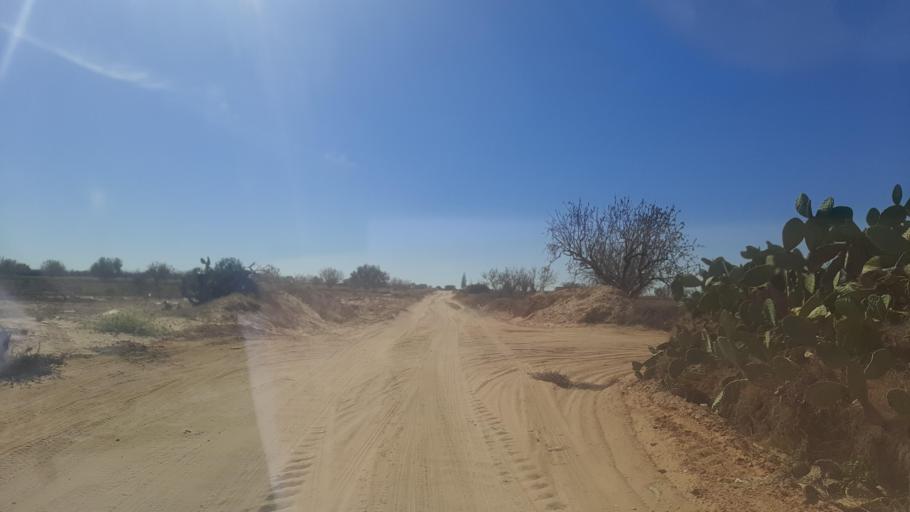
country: TN
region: Safaqis
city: Sfax
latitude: 34.8521
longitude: 10.5625
